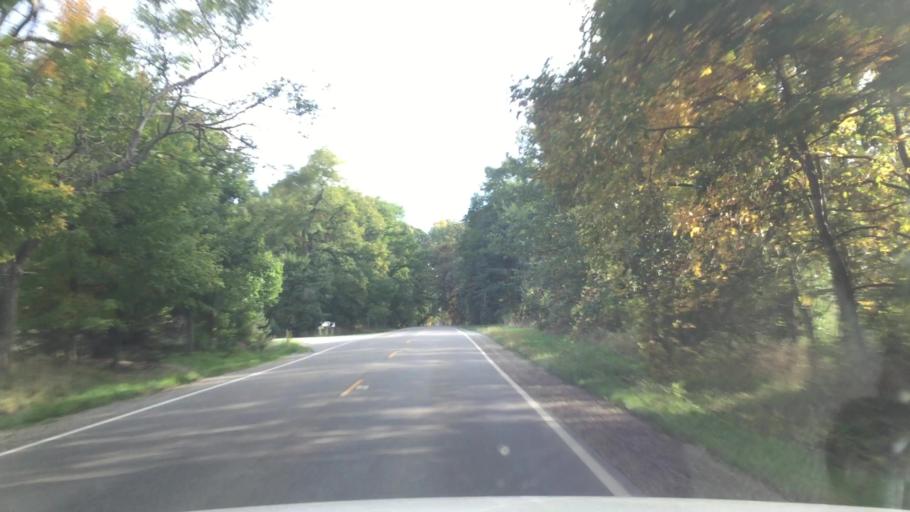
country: US
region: Michigan
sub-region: Genesee County
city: Fenton
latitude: 42.6729
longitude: -83.7018
